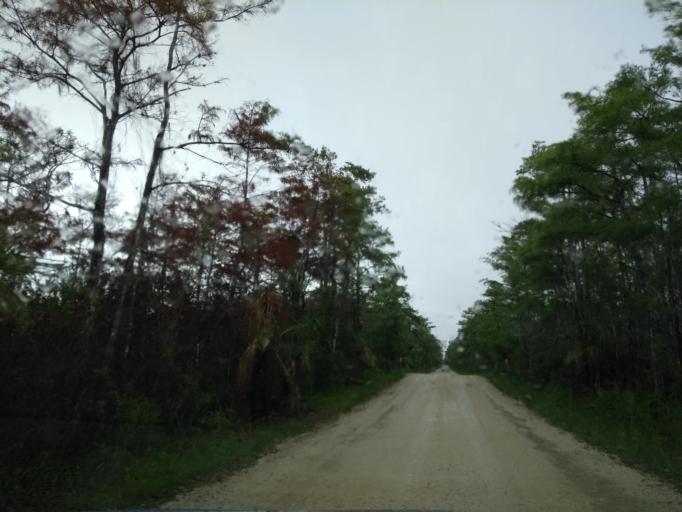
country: US
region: Florida
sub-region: Miami-Dade County
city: The Hammocks
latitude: 25.7602
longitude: -81.0432
